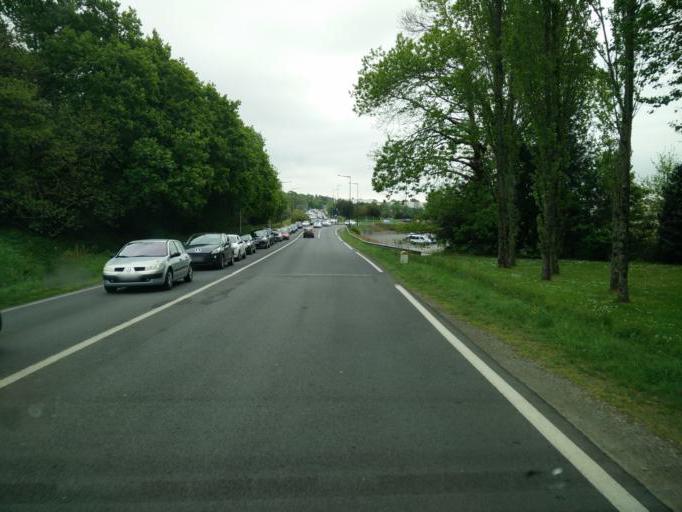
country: FR
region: Brittany
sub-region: Departement du Finistere
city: Concarneau
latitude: 47.8807
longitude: -3.9086
